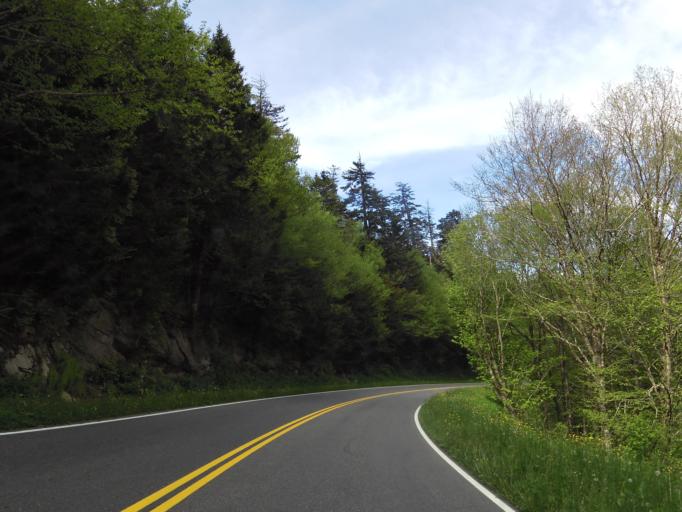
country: US
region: Tennessee
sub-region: Sevier County
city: Gatlinburg
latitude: 35.5959
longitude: -83.4567
